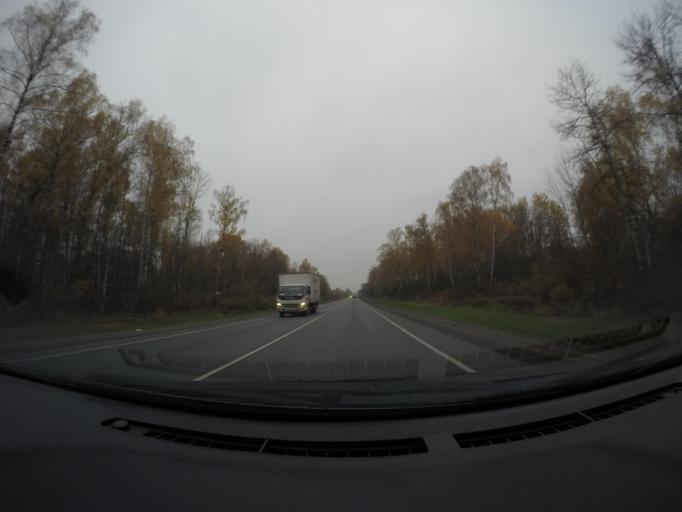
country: RU
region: Moskovskaya
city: Yakovlevskoye
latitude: 55.3669
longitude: 38.0577
